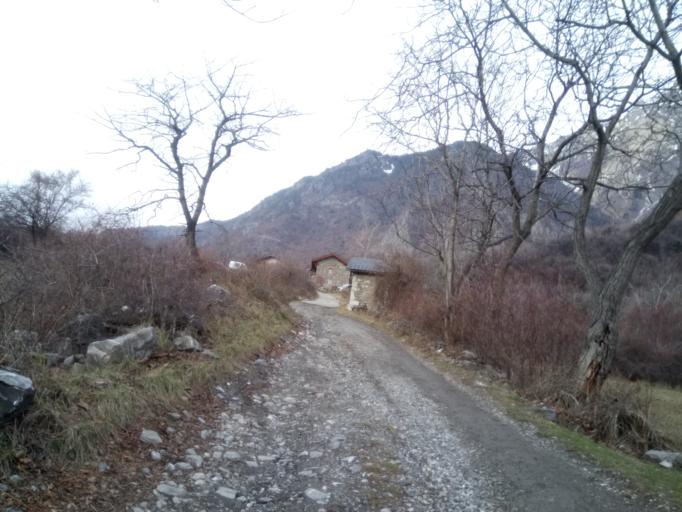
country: FR
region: Rhone-Alpes
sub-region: Departement de la Savoie
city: Saint-Michel-de-Maurienne
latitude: 45.2509
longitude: 6.4272
